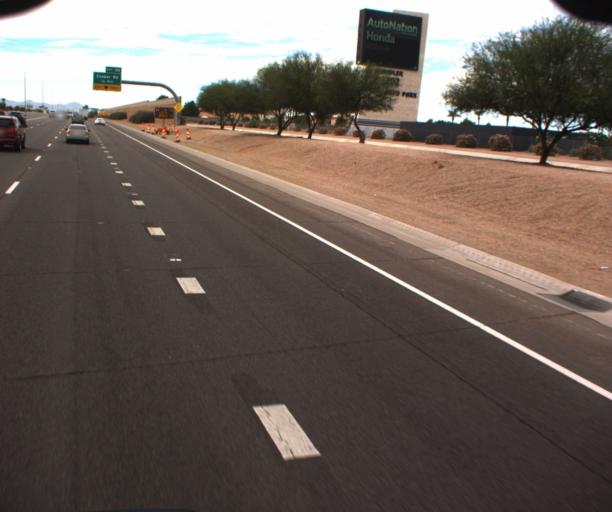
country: US
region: Arizona
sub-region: Maricopa County
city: Chandler
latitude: 33.2830
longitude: -111.7955
